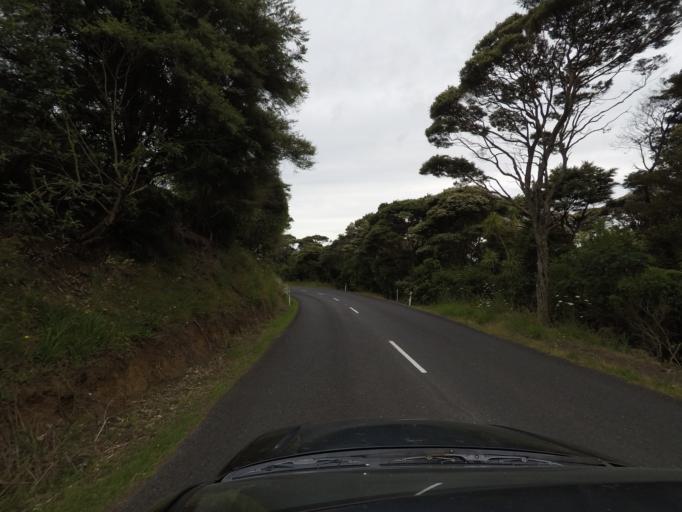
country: NZ
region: Waikato
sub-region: Waikato District
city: Raglan
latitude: -37.8257
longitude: 174.8151
